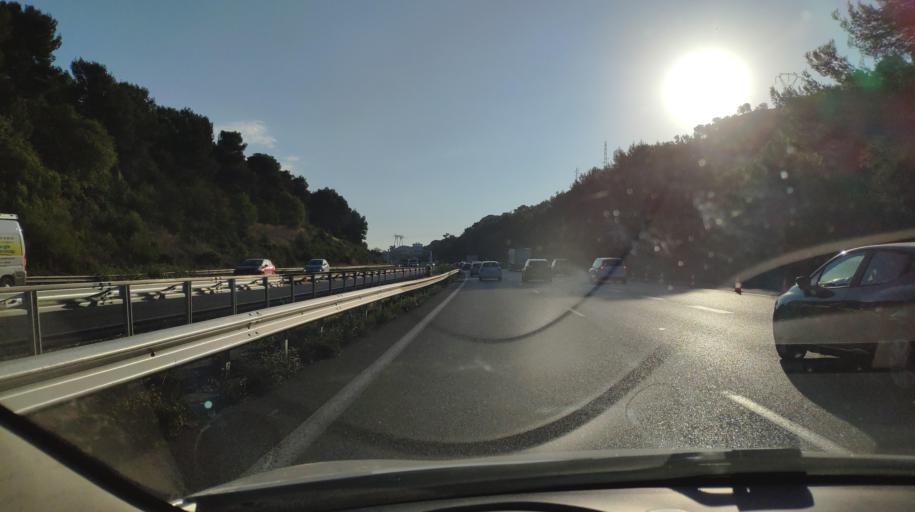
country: FR
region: Provence-Alpes-Cote d'Azur
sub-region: Departement des Bouches-du-Rhone
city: Les Pennes-Mirabeau
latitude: 43.4034
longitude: 5.3089
